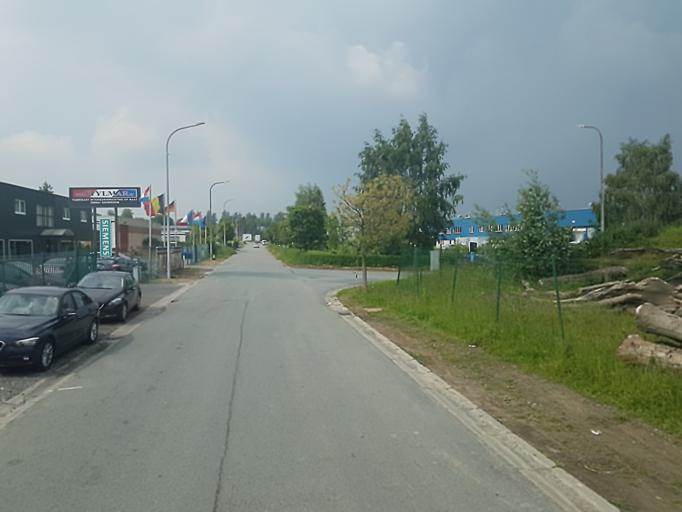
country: BE
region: Flanders
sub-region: Provincie Oost-Vlaanderen
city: Geraardsbergen
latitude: 50.7912
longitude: 3.8769
